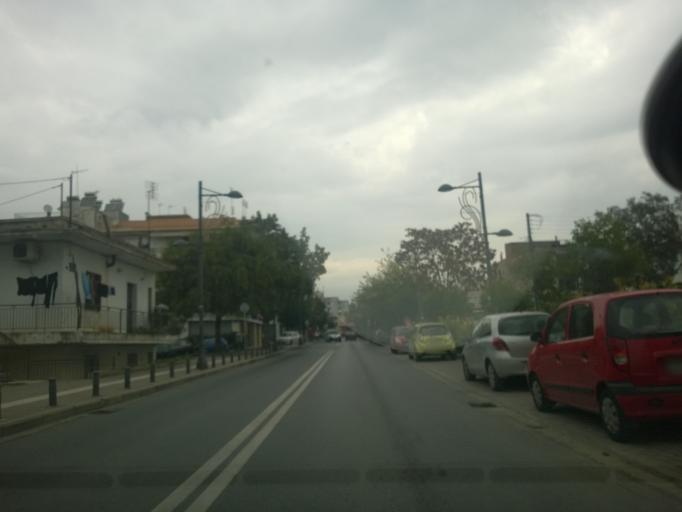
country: GR
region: Central Macedonia
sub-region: Nomos Thessalonikis
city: Stavroupoli
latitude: 40.6711
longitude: 22.9336
